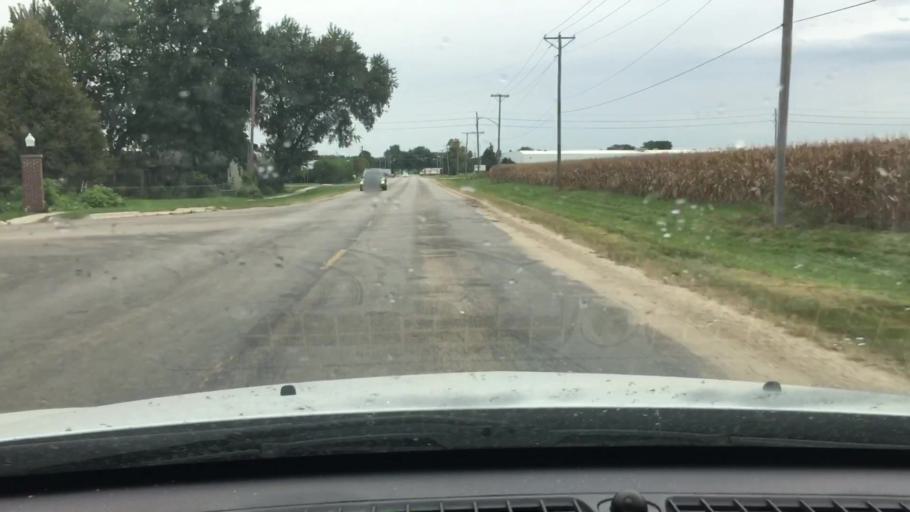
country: US
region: Illinois
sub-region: Ogle County
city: Rochelle
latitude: 41.9036
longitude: -89.0539
